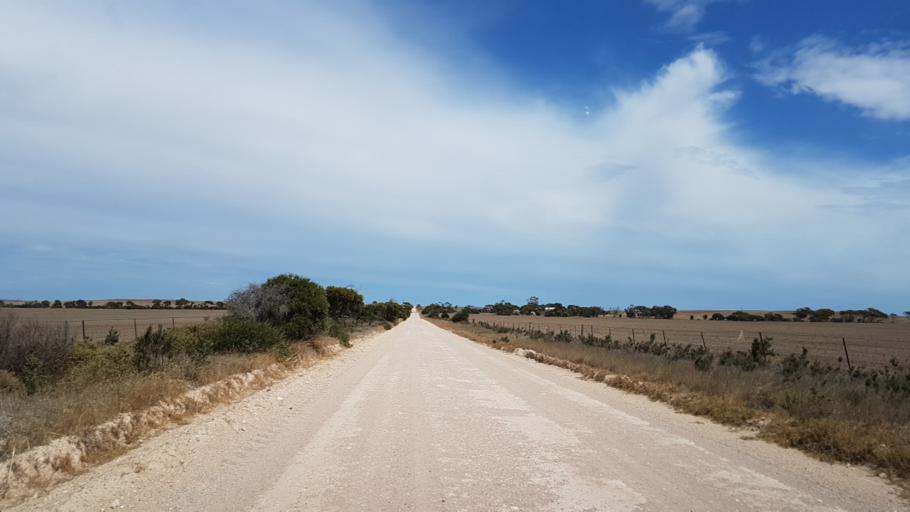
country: AU
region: South Australia
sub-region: Yorke Peninsula
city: Ardrossan
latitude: -34.3984
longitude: 137.9239
